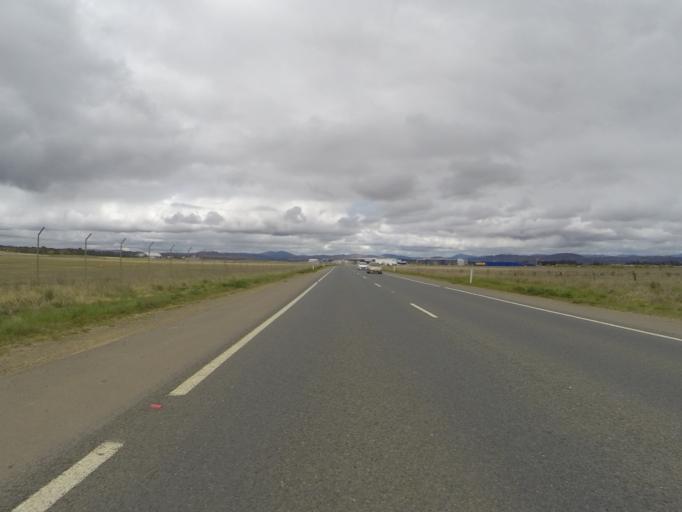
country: AU
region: Australian Capital Territory
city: Canberra
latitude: -35.2871
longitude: 149.1939
